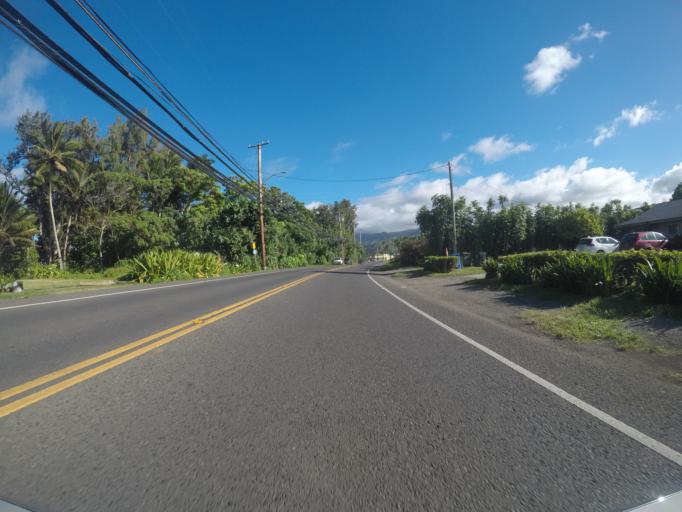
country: US
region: Hawaii
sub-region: Honolulu County
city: La'ie
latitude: 21.6455
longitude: -157.9198
